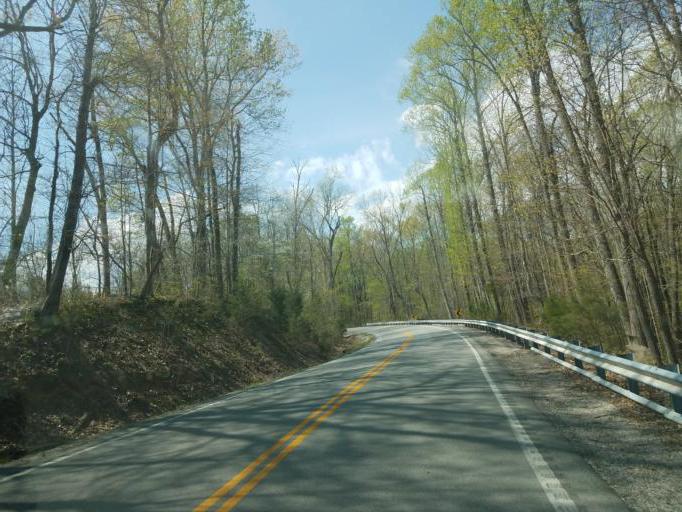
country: US
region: Kentucky
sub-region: Edmonson County
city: Brownsville
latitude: 37.1398
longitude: -86.4112
